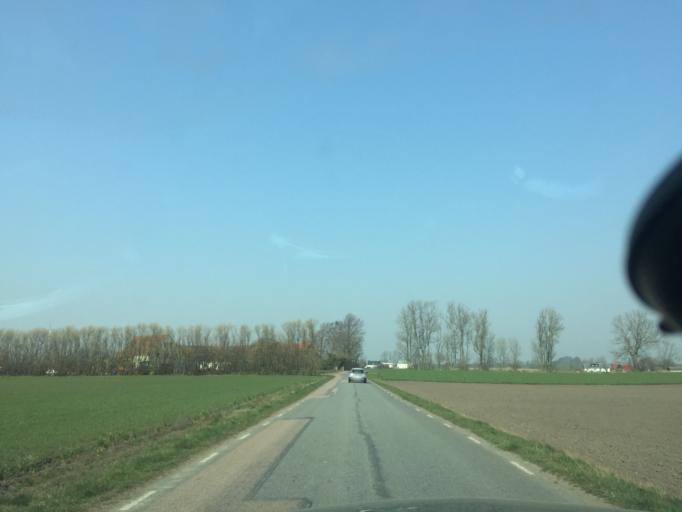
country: SE
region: Skane
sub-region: Simrishamns Kommun
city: Simrishamn
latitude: 55.4635
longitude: 14.2091
